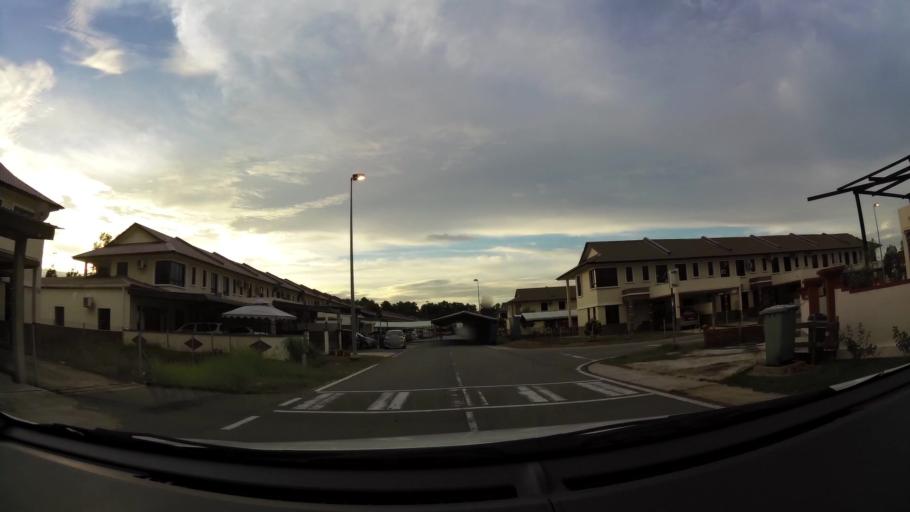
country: BN
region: Brunei and Muara
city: Bandar Seri Begawan
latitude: 4.9941
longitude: 114.9880
